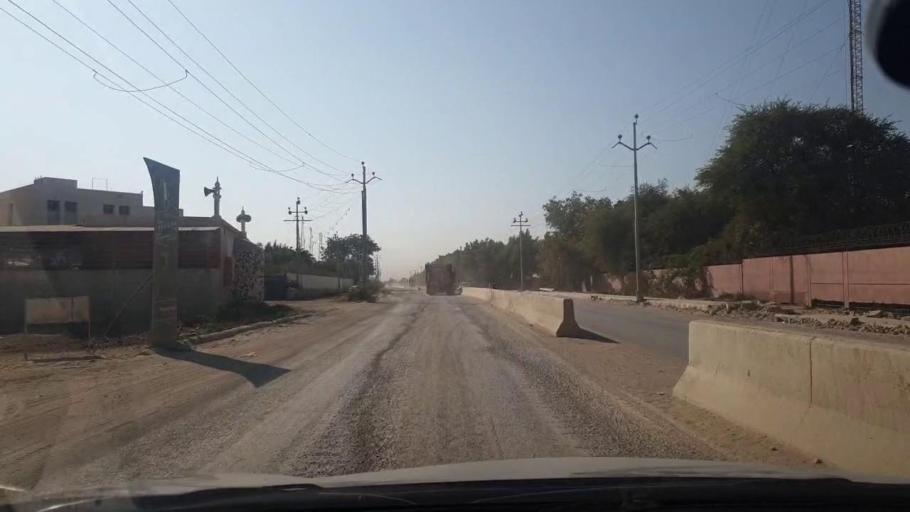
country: PK
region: Sindh
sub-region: Karachi District
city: Karachi
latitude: 25.0846
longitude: 67.0126
